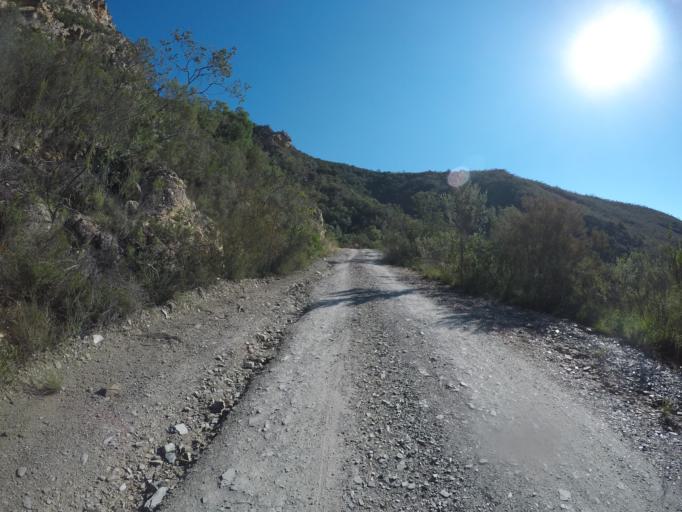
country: ZA
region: Eastern Cape
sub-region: Cacadu District Municipality
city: Kareedouw
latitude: -33.6567
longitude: 24.5056
